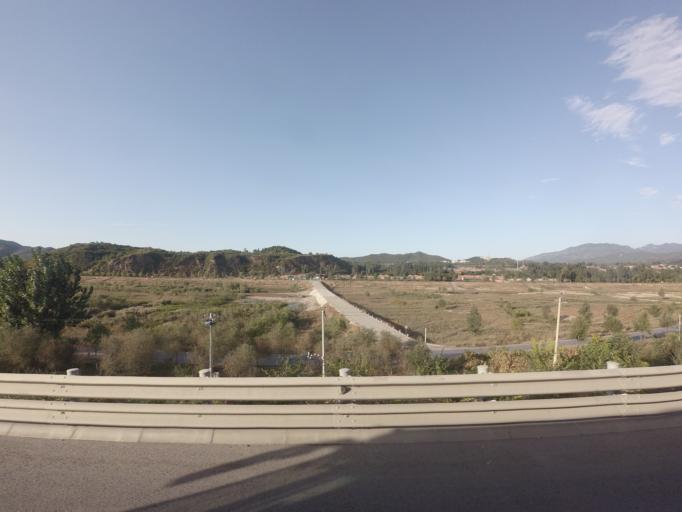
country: CN
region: Beijing
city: Jugezhuang
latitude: 40.3950
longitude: 116.9456
